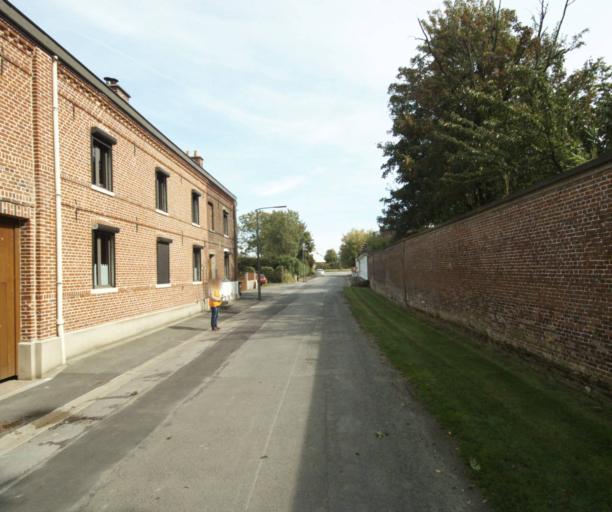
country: FR
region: Nord-Pas-de-Calais
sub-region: Departement du Nord
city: Ennetieres-en-Weppes
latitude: 50.6188
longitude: 2.9362
